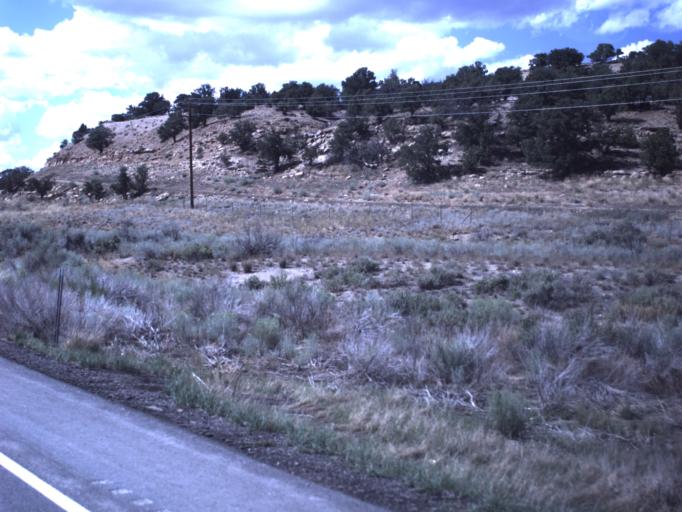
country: US
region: Utah
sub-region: Duchesne County
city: Duchesne
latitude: 40.1728
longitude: -110.5865
